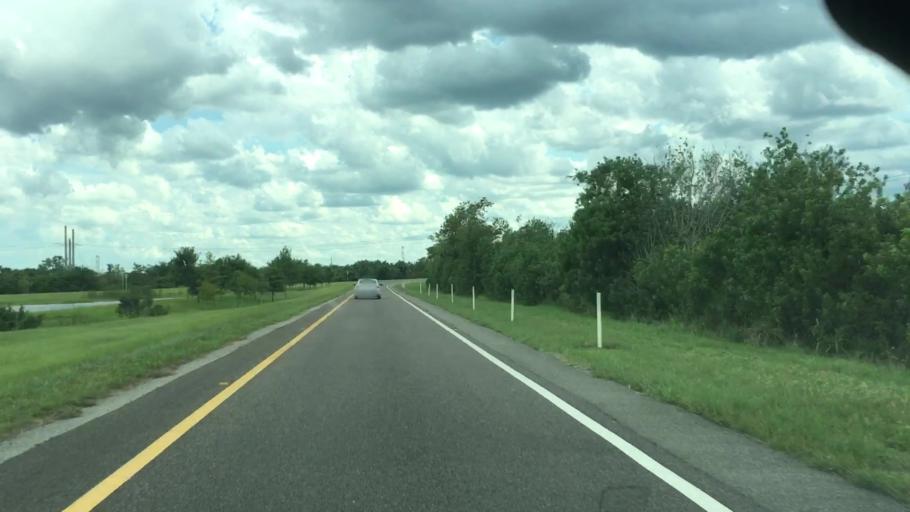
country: US
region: Florida
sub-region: Brevard County
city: Port Saint John
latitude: 28.4997
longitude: -80.8419
